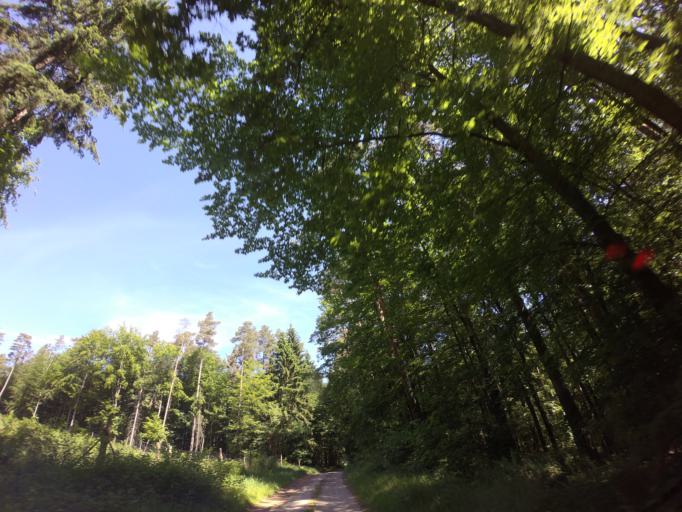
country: PL
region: West Pomeranian Voivodeship
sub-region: Powiat choszczenski
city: Recz
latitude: 53.3137
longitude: 15.6028
